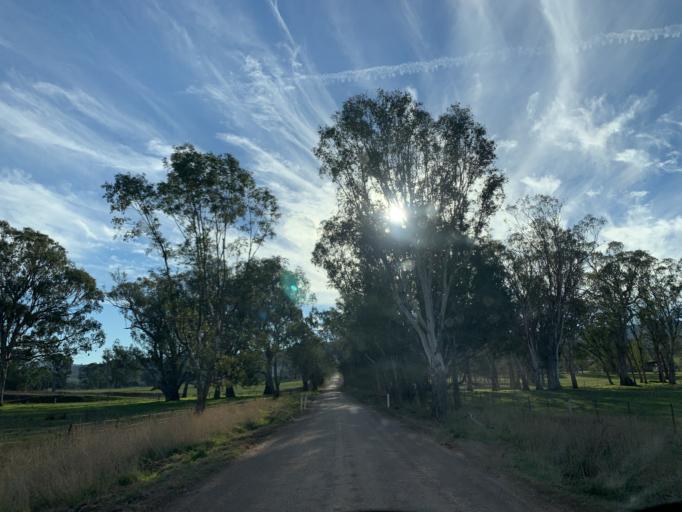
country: AU
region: Victoria
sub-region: Mansfield
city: Mansfield
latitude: -36.9625
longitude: 146.1070
